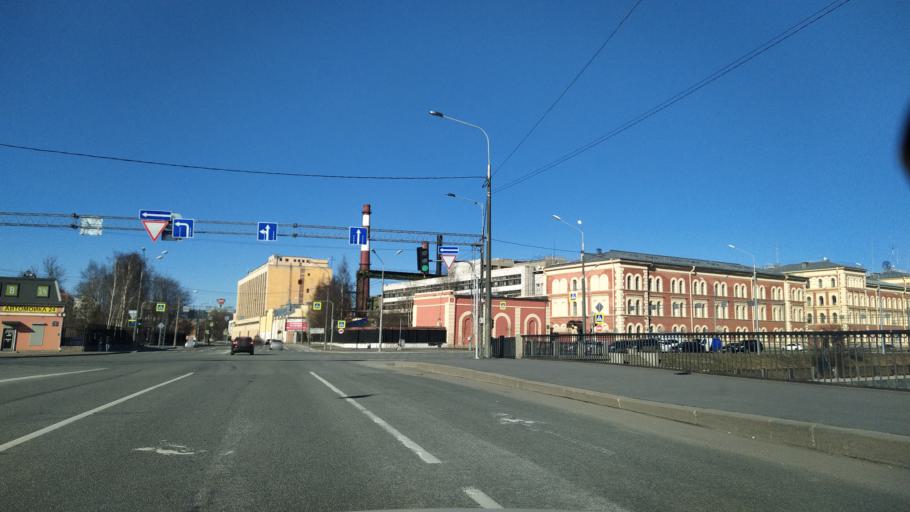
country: RU
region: St.-Petersburg
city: Centralniy
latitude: 59.9149
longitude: 30.3748
